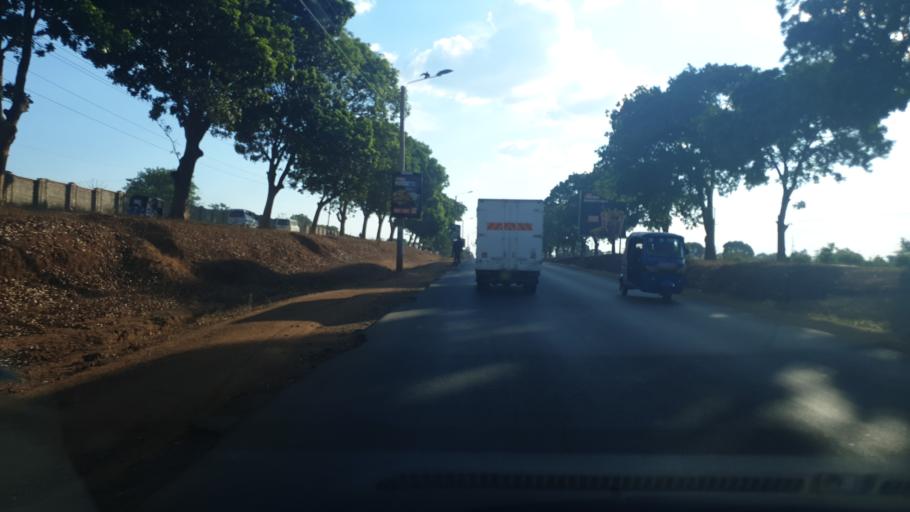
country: MW
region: Central Region
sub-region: Lilongwe District
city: Lilongwe
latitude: -13.9731
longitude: 33.7818
